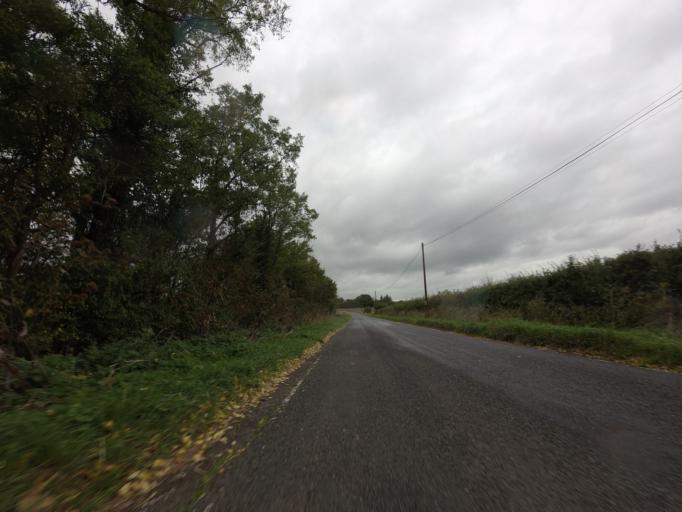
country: GB
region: England
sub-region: Cambridgeshire
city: Comberton
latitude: 52.1698
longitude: -0.0131
